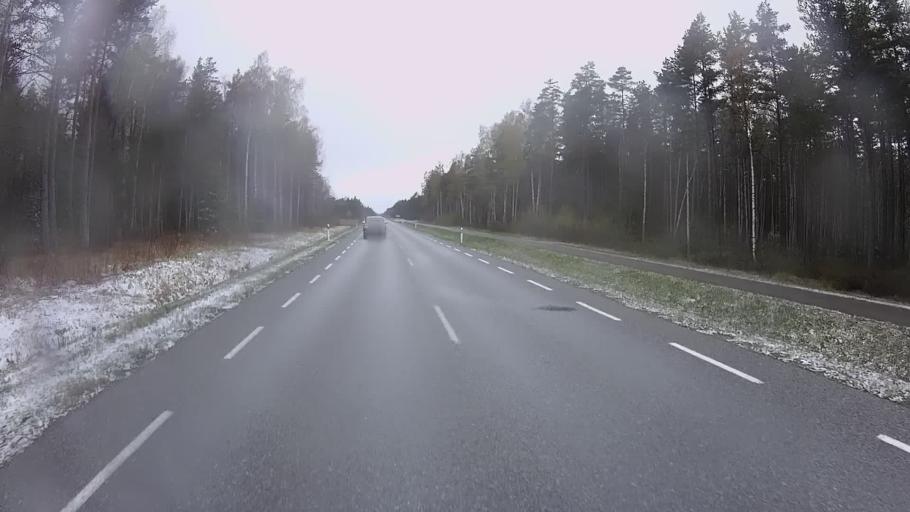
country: EE
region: Hiiumaa
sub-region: Kaerdla linn
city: Kardla
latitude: 59.0099
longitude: 22.6334
